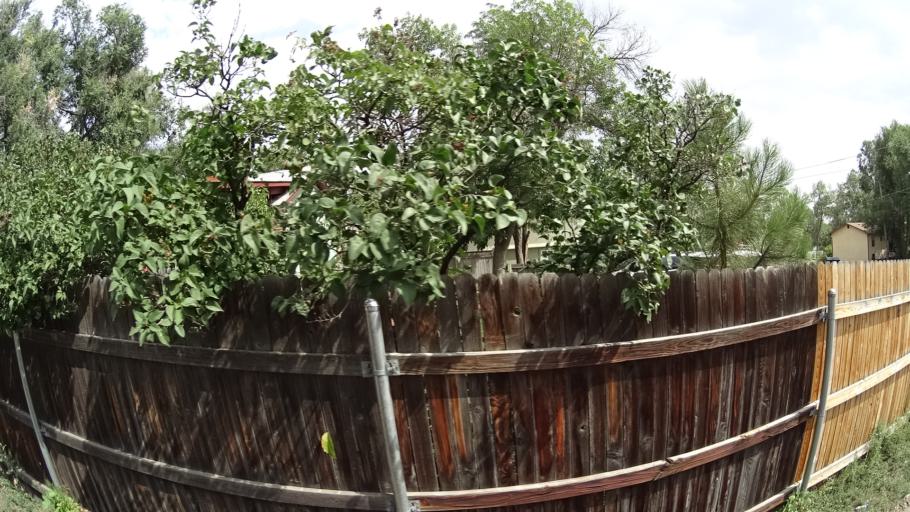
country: US
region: Colorado
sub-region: El Paso County
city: Colorado Springs
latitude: 38.8439
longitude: -104.7922
